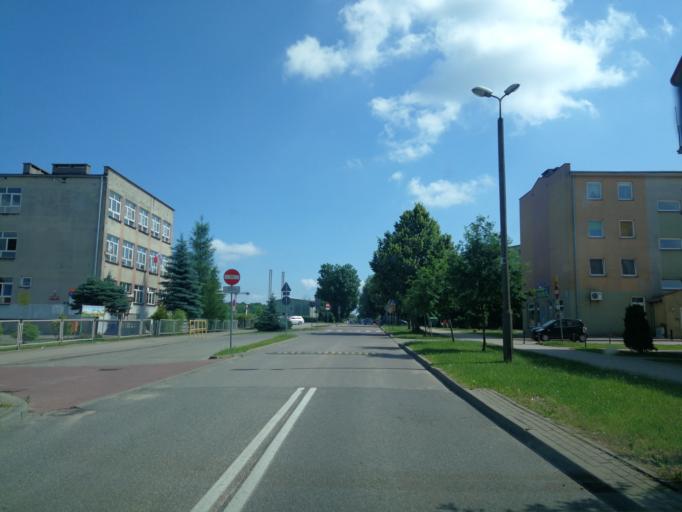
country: PL
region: Warmian-Masurian Voivodeship
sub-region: Powiat ilawski
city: Lubawa
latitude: 53.5013
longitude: 19.7508
